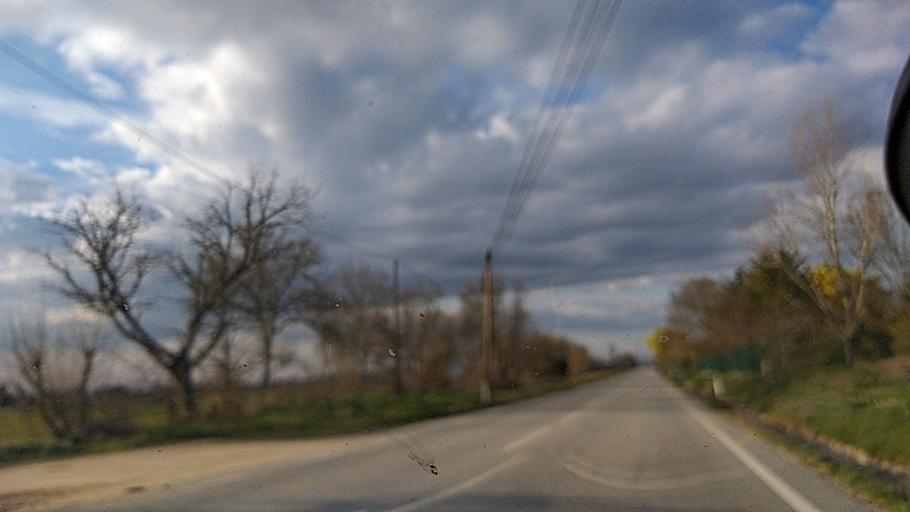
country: ES
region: Castille and Leon
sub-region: Provincia de Salamanca
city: Aldea del Obispo
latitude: 40.7069
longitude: -6.8967
